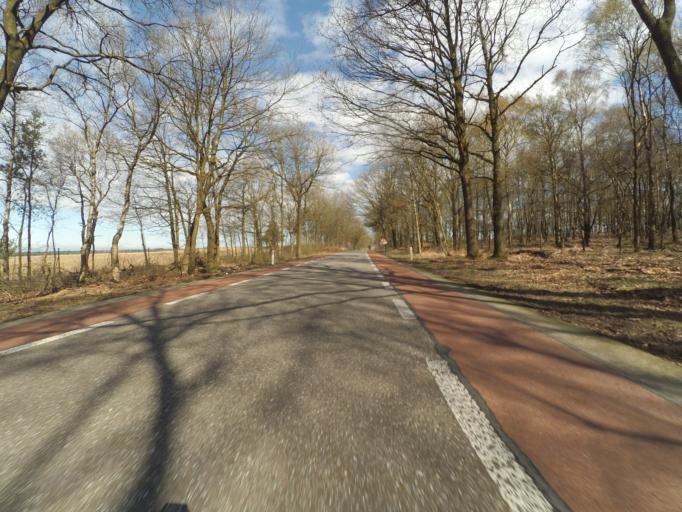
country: NL
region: Gelderland
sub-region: Gemeente Arnhem
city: Hoogkamp
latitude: 52.0834
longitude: 5.8797
